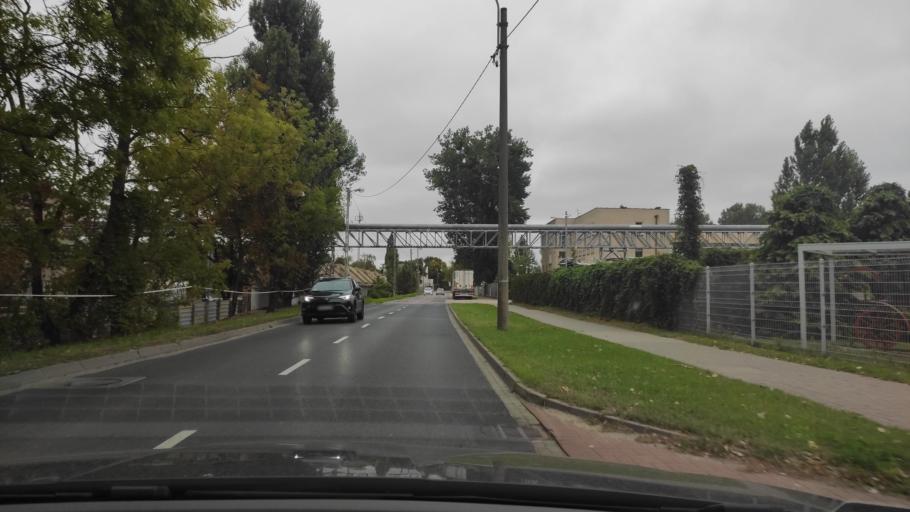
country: PL
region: Greater Poland Voivodeship
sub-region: Poznan
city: Poznan
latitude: 52.4158
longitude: 16.9753
